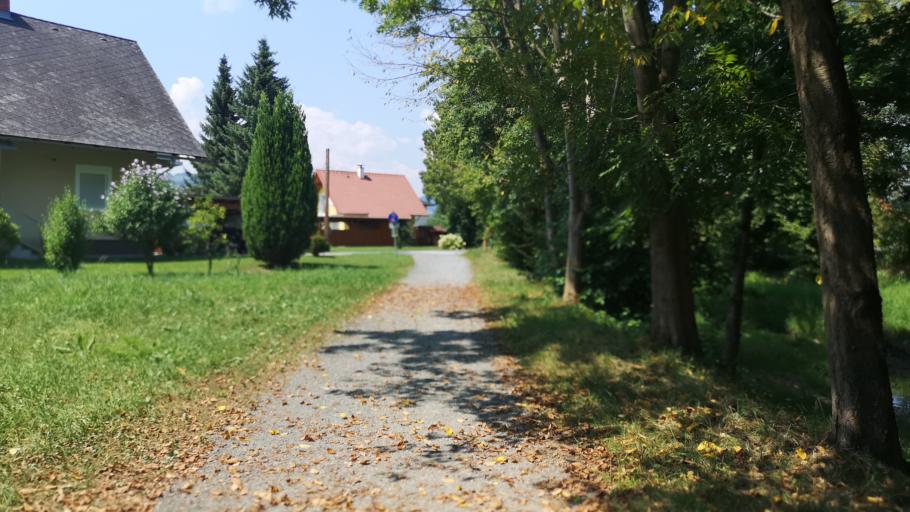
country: AT
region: Styria
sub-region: Politischer Bezirk Deutschlandsberg
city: Deutschlandsberg
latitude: 46.8239
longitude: 15.2450
